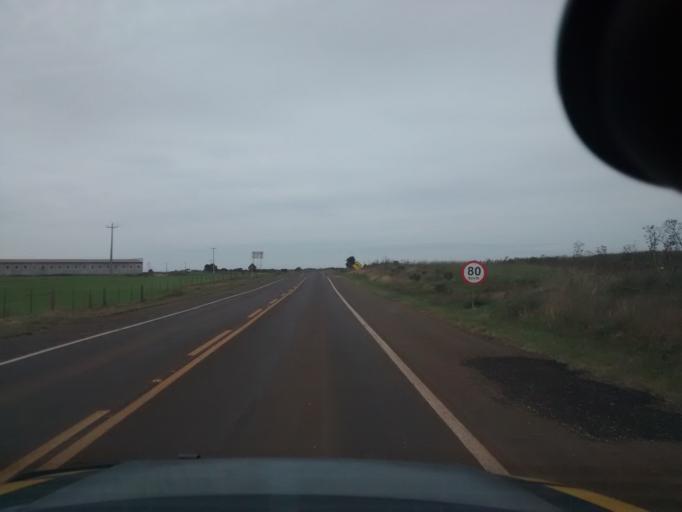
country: BR
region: Rio Grande do Sul
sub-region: Vacaria
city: Vacaria
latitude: -28.4294
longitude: -51.0220
